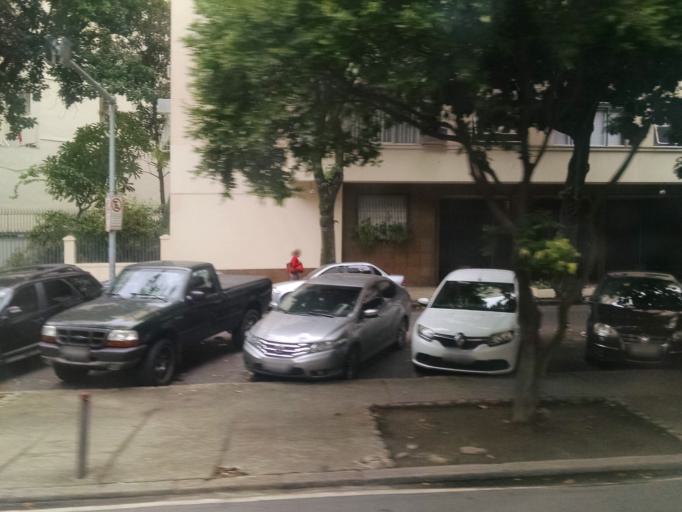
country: BR
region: Rio de Janeiro
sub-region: Rio De Janeiro
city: Rio de Janeiro
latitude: -22.9554
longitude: -43.1978
